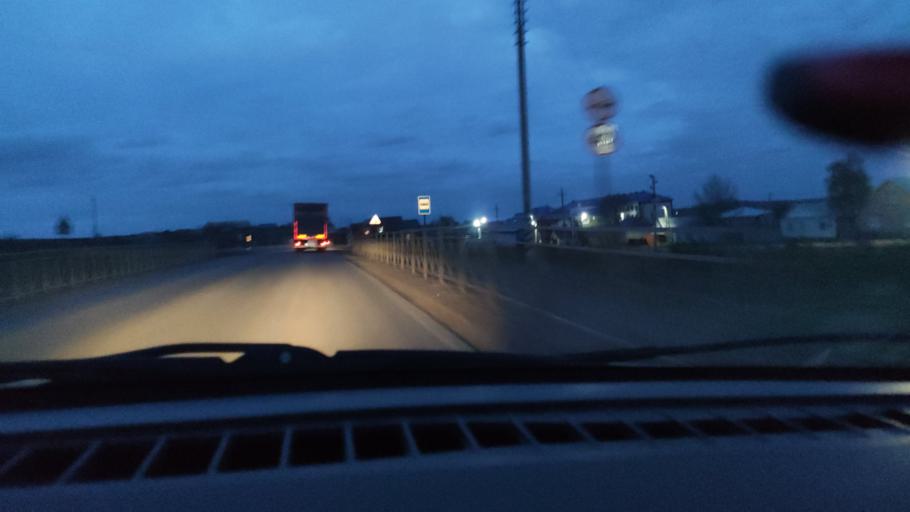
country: RU
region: Orenburg
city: Tatarskaya Kargala
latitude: 51.9494
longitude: 55.1800
